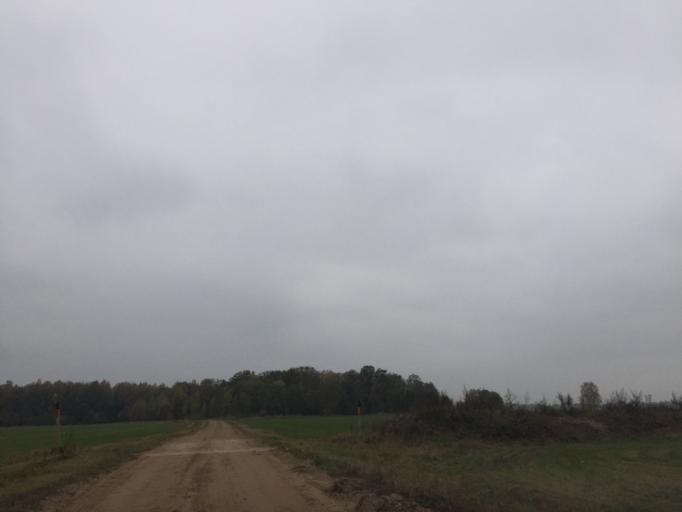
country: LV
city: Tireli
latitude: 56.6732
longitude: 23.4837
